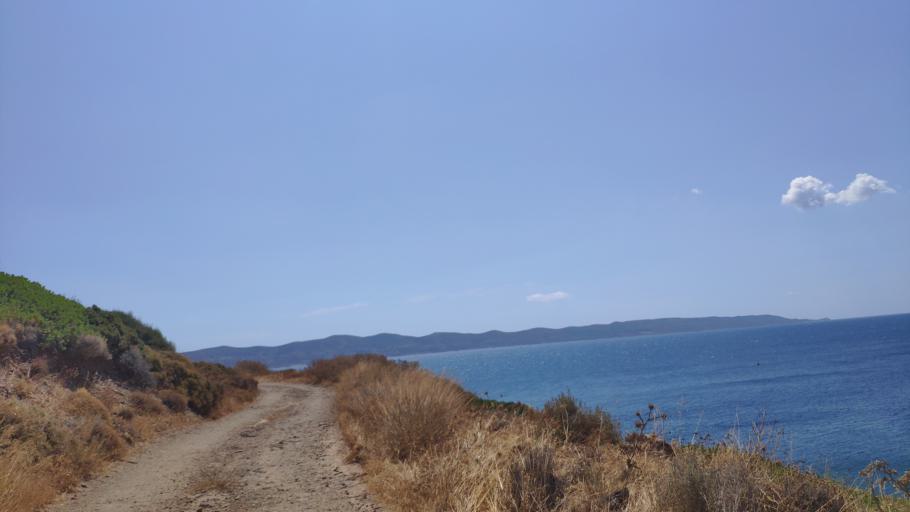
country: GR
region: Attica
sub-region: Nomarchia Anatolikis Attikis
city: Lavrio
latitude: 37.7442
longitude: 24.0764
